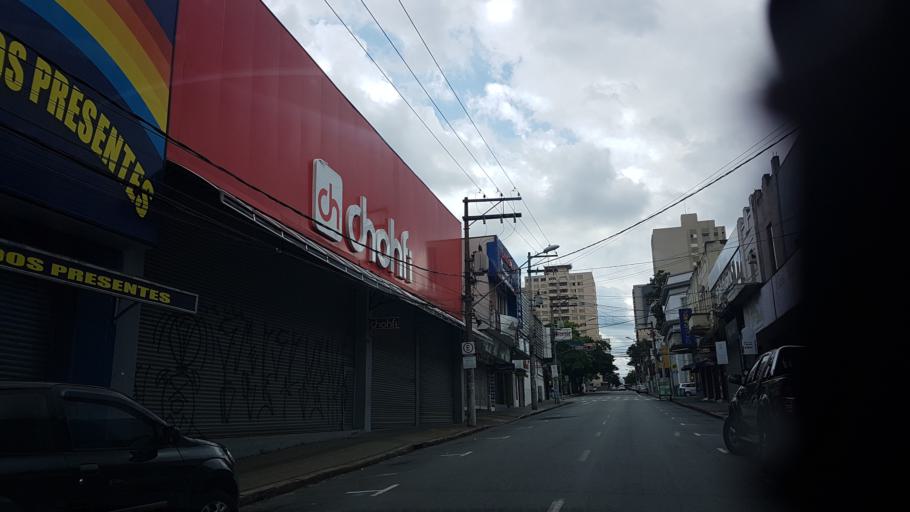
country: BR
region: Sao Paulo
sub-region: Limeira
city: Limeira
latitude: -22.5627
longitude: -47.4012
